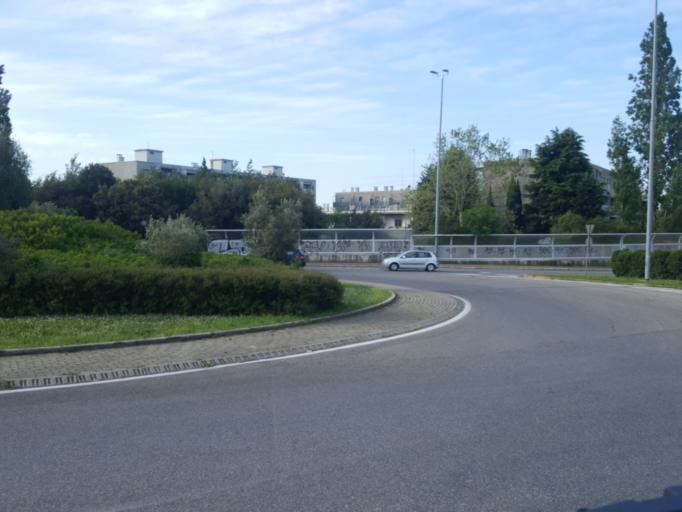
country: IT
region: Tuscany
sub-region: Province of Florence
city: Calenzano
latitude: 43.8442
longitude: 11.1808
